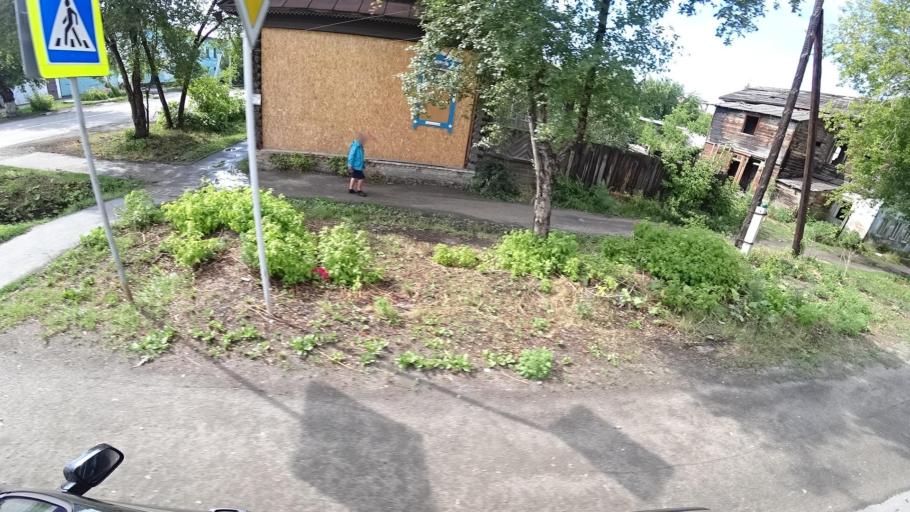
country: RU
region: Sverdlovsk
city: Kamyshlov
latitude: 56.8426
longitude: 62.7157
